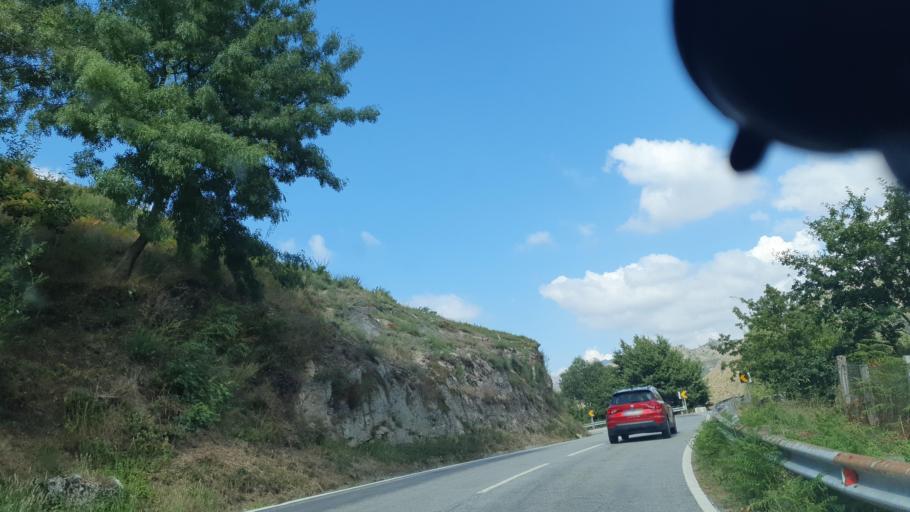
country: PT
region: Braga
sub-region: Terras de Bouro
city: Terras de Bouro
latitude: 41.7247
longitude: -8.2172
